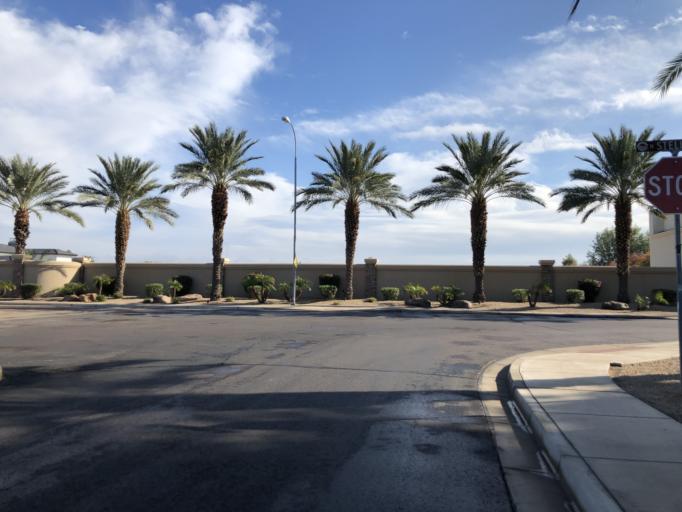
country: US
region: Arizona
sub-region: Maricopa County
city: Chandler
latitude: 33.3040
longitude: -111.9190
